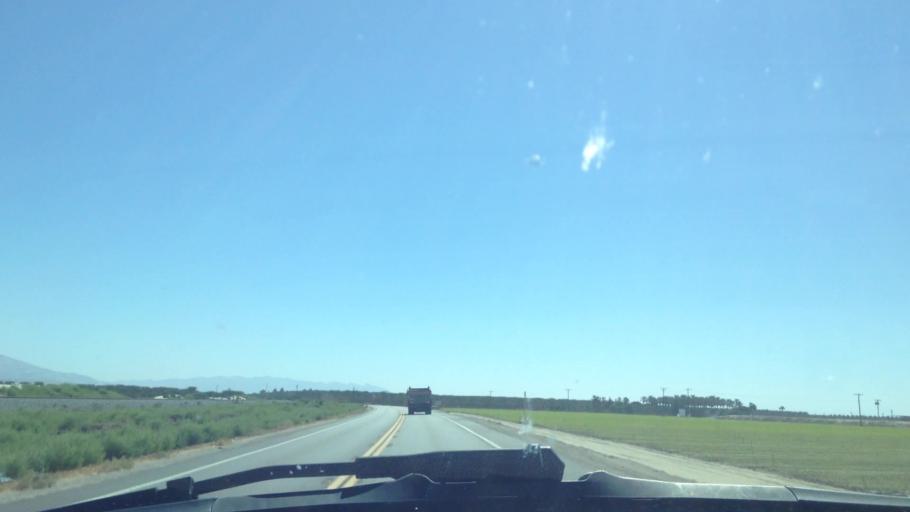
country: US
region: California
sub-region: Riverside County
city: Mecca
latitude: 33.5384
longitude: -116.0254
